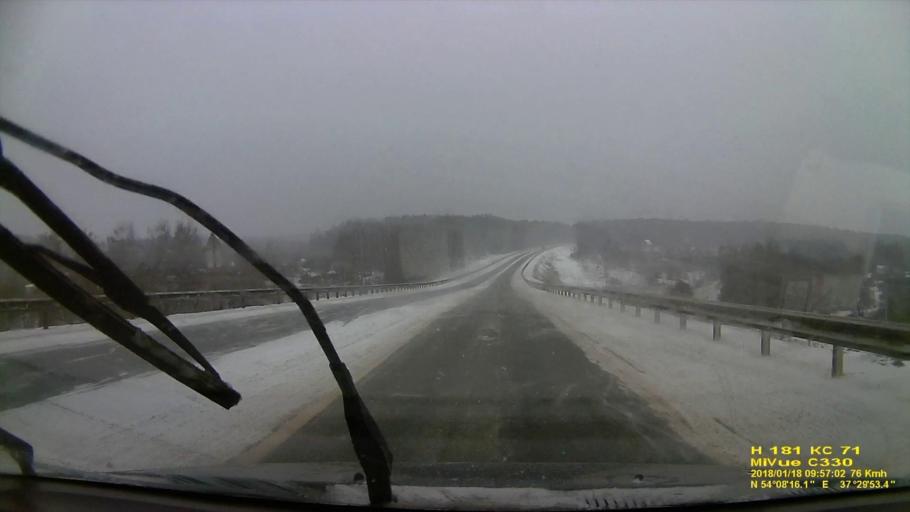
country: RU
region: Tula
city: Kosaya Gora
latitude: 54.1376
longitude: 37.4981
